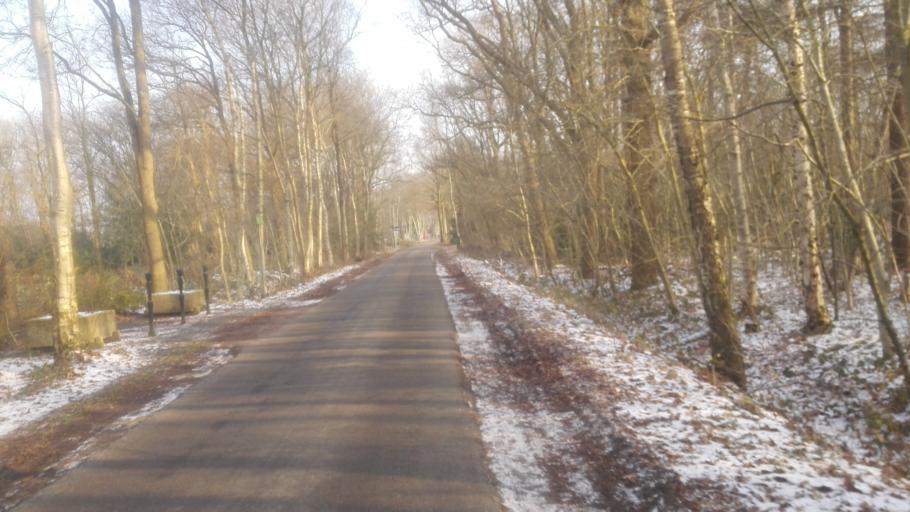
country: NL
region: Friesland
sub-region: Gemeente Heerenveen
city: Nieuwehorne
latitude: 52.9546
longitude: 6.0790
